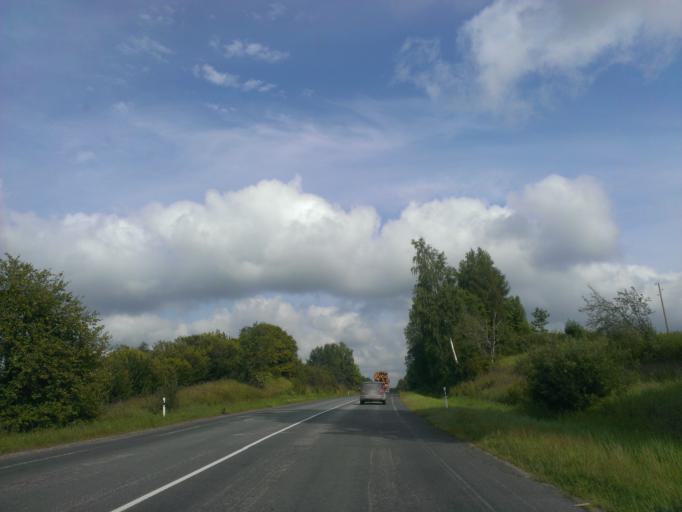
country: LV
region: Priekuli
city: Priekuli
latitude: 57.2554
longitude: 25.3526
